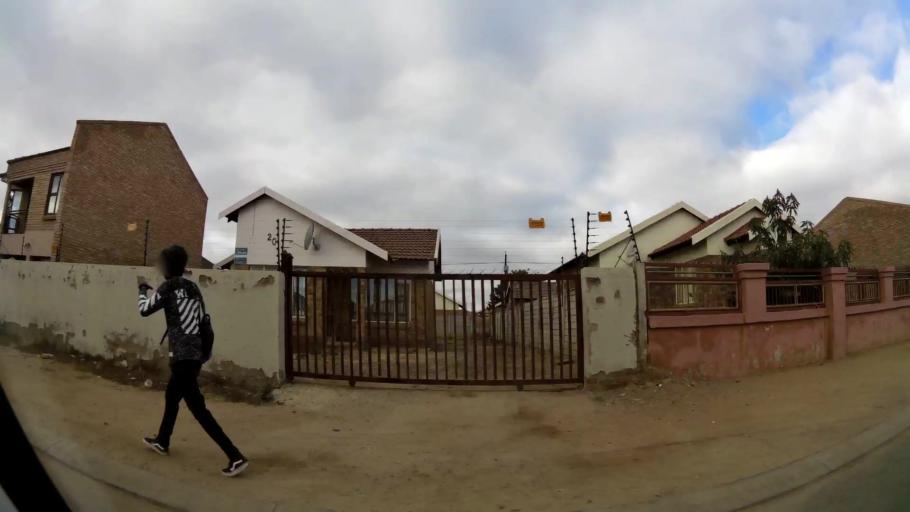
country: ZA
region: Limpopo
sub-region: Capricorn District Municipality
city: Polokwane
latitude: -23.9255
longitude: 29.4458
